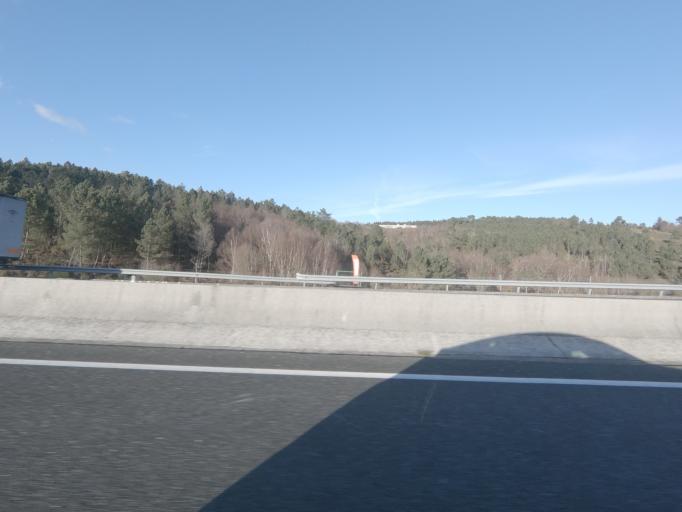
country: ES
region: Galicia
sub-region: Provincia de Pontevedra
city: Lalin
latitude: 42.6014
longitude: -8.0953
